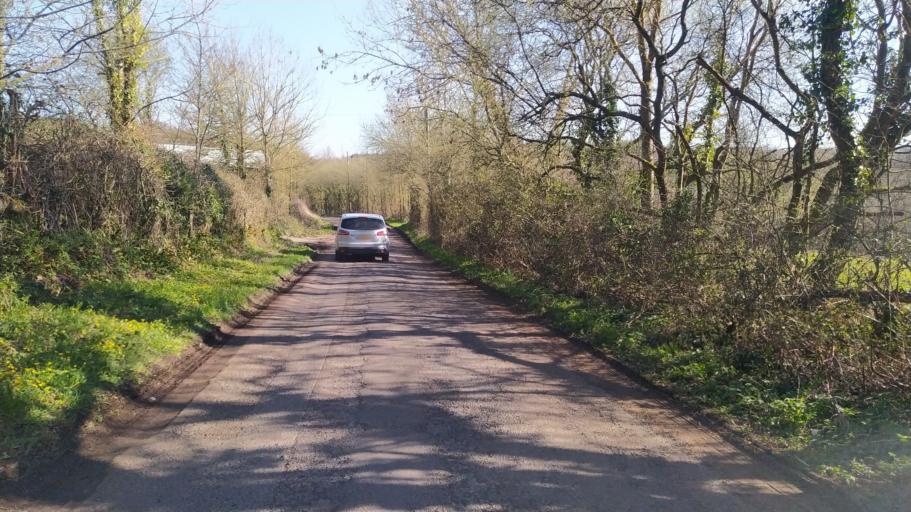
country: GB
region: England
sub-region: Dorset
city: Verwood
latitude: 50.9012
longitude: -1.9076
